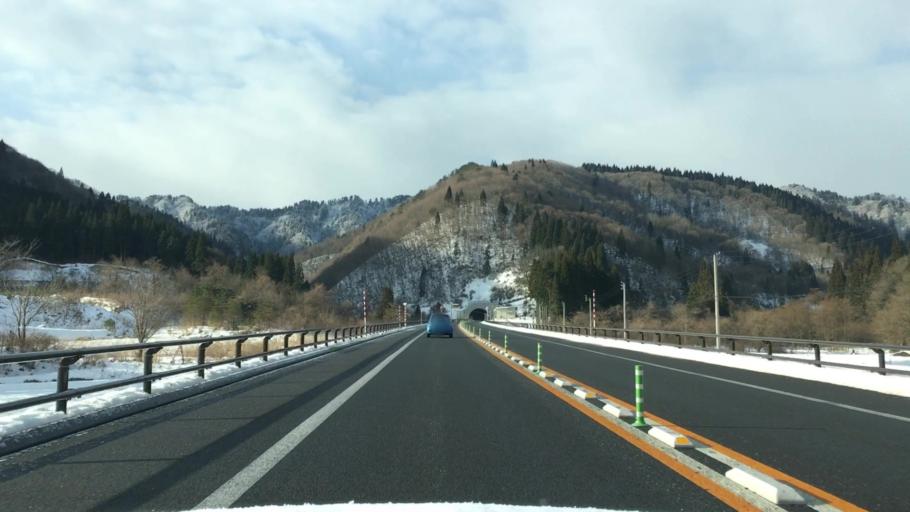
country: JP
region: Akita
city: Odate
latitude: 40.2323
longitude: 140.4931
